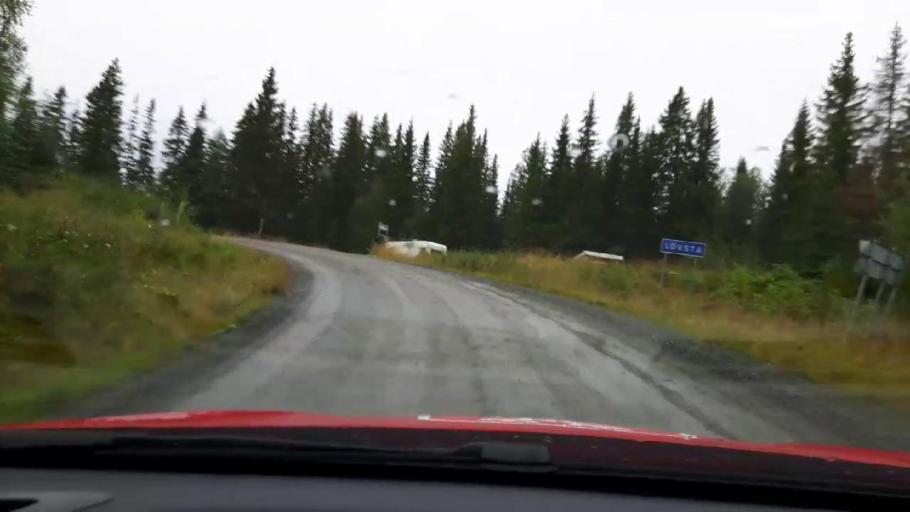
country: SE
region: Jaemtland
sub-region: Are Kommun
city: Are
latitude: 63.4327
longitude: 12.8011
